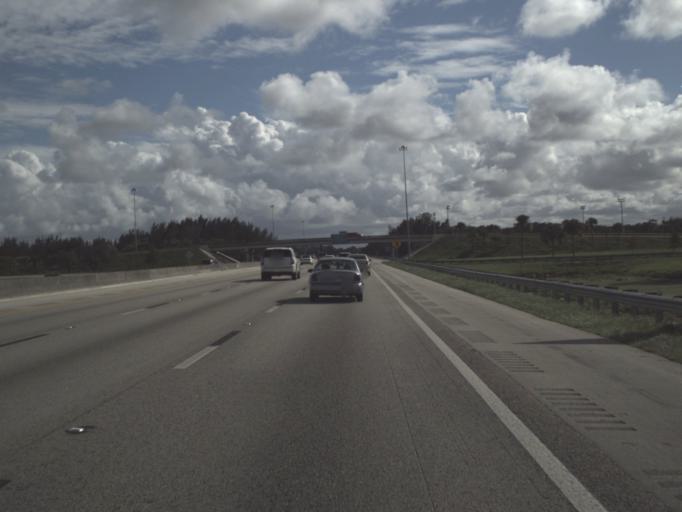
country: US
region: Florida
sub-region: Broward County
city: Coconut Creek
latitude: 26.2736
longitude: -80.1690
